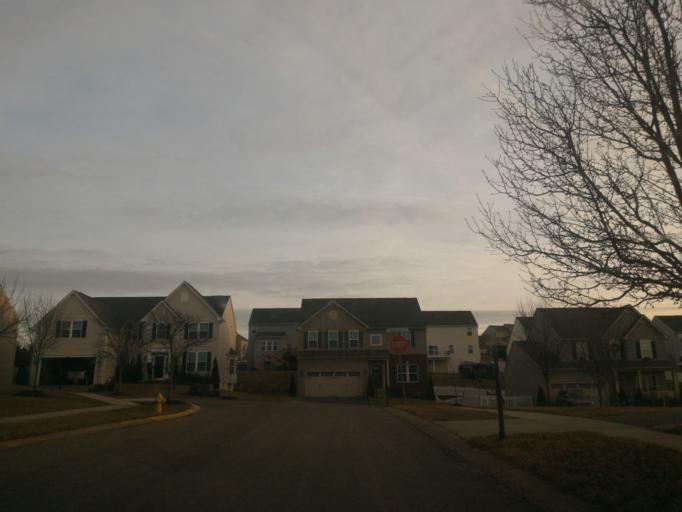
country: US
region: Pennsylvania
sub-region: York County
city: Loganville
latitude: 39.8619
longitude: -76.7200
